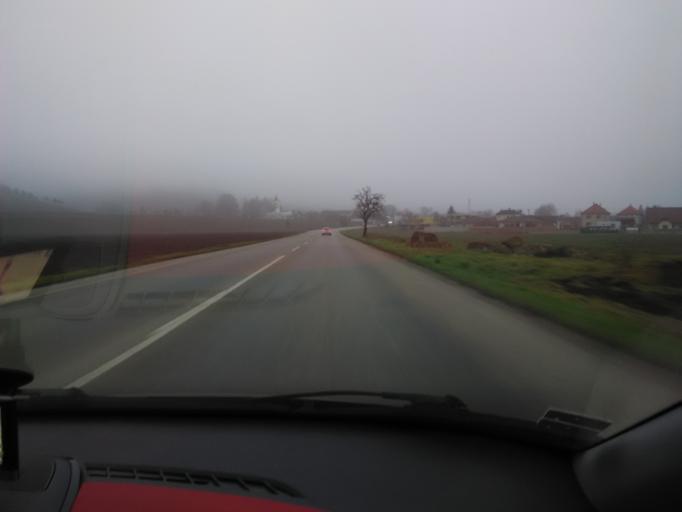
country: SK
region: Trenciansky
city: Nova Dubnica
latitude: 48.9171
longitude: 18.0979
